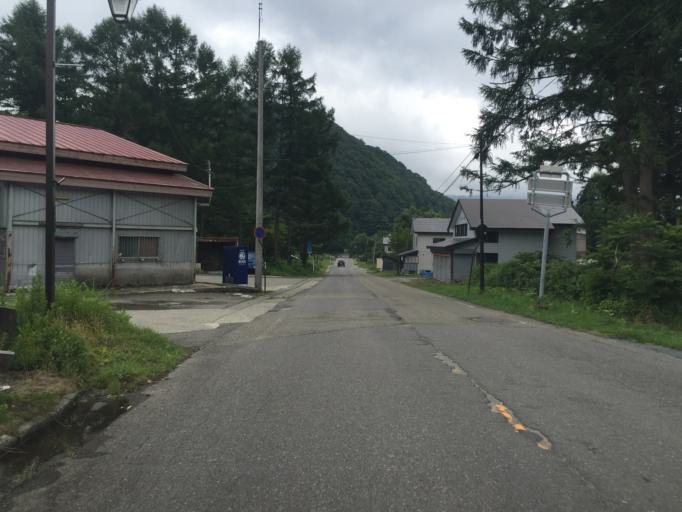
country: JP
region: Fukushima
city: Inawashiro
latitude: 37.7252
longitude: 140.0631
